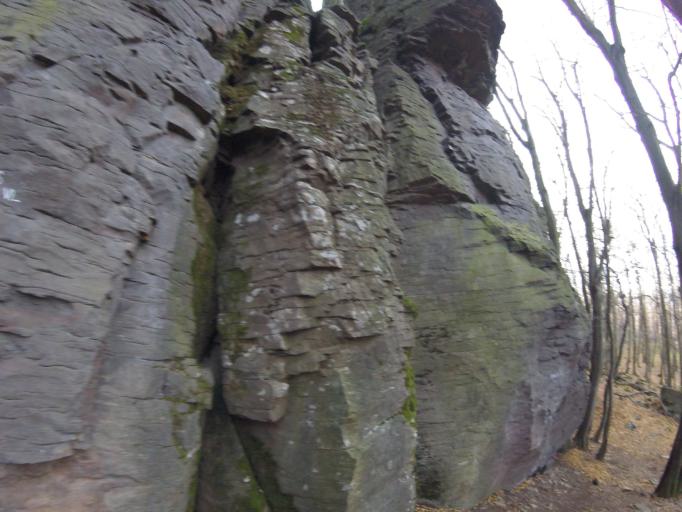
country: HU
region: Heves
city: Abasar
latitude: 47.8296
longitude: 20.0031
